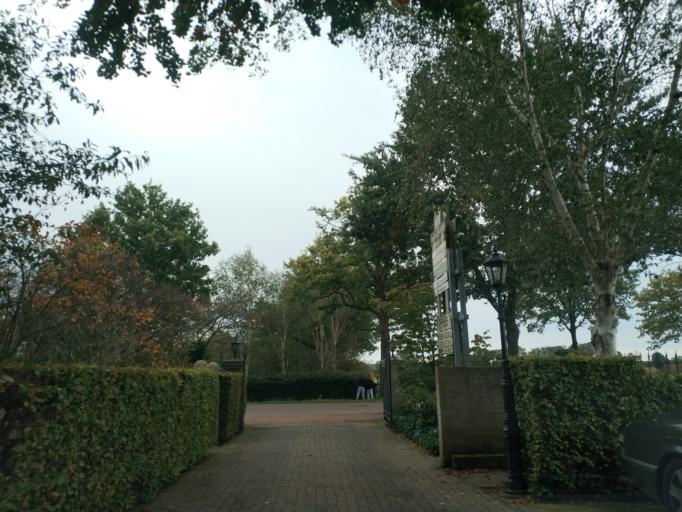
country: NL
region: North Brabant
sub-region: Gemeente Goirle
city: Goirle
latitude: 51.5205
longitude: 5.0129
